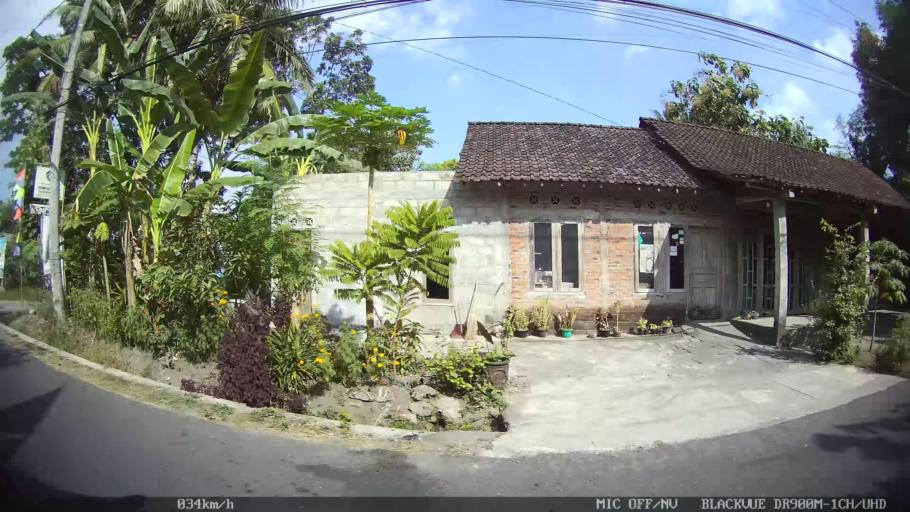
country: ID
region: Daerah Istimewa Yogyakarta
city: Kasihan
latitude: -7.8417
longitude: 110.3107
